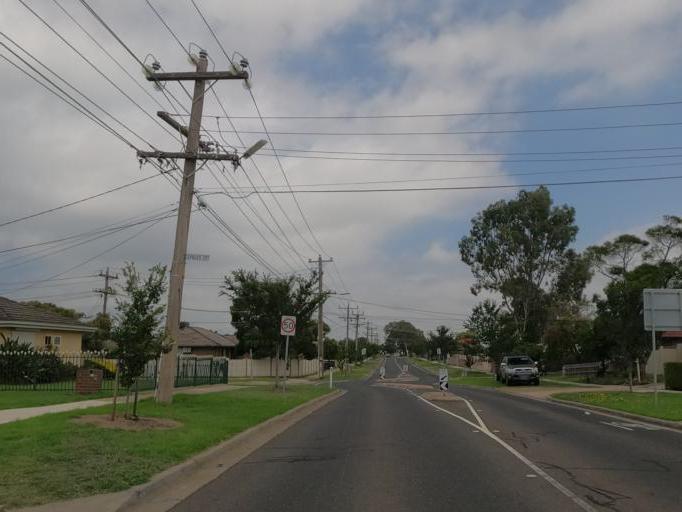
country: AU
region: Victoria
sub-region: Hume
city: Gladstone Park
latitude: -37.6907
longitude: 144.8973
